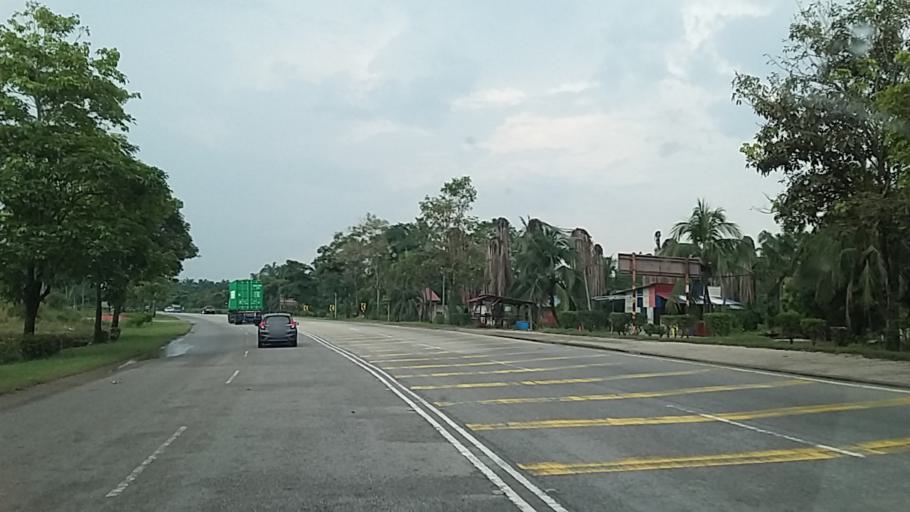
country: MY
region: Johor
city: Parit Raja
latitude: 1.8755
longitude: 103.1417
